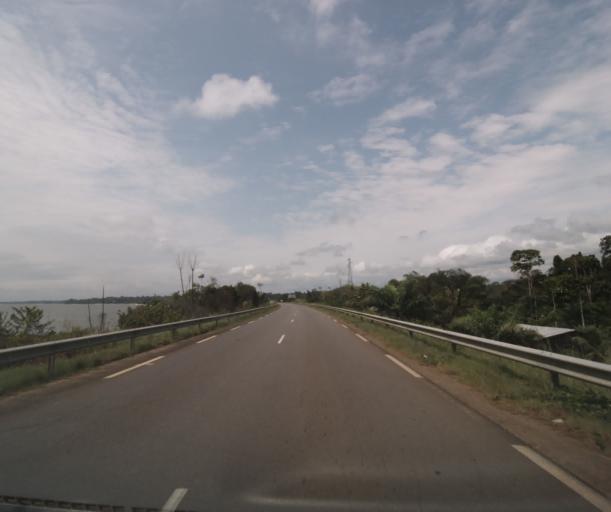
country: CM
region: South Province
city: Kribi
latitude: 3.0072
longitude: 9.9481
